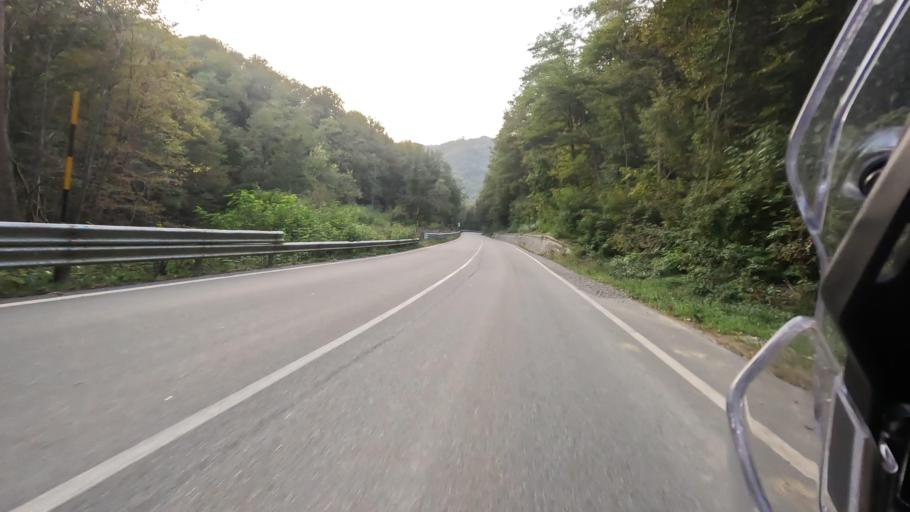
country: IT
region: Liguria
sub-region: Provincia di Savona
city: Osteria dei Cacciatori-Stella
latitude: 44.4455
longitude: 8.4820
